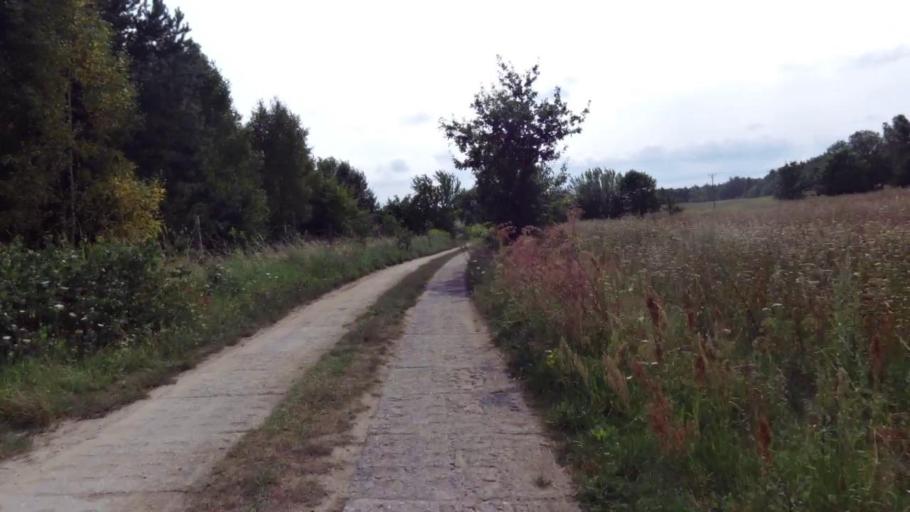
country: PL
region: West Pomeranian Voivodeship
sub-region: Powiat drawski
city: Czaplinek
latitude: 53.5713
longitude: 16.2435
